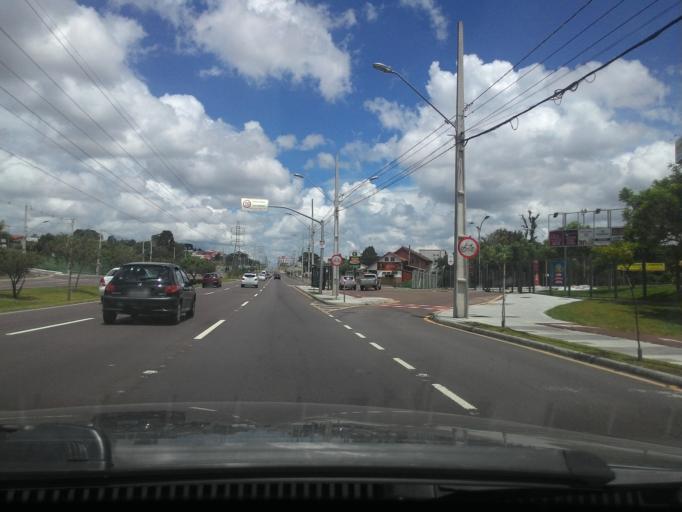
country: BR
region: Parana
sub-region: Pinhais
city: Pinhais
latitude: -25.4815
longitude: -49.2254
